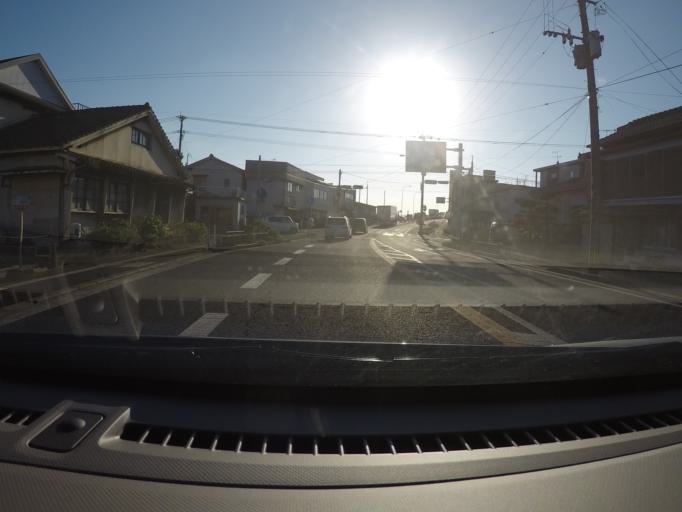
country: JP
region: Kagoshima
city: Izumi
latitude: 32.1165
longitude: 130.3396
